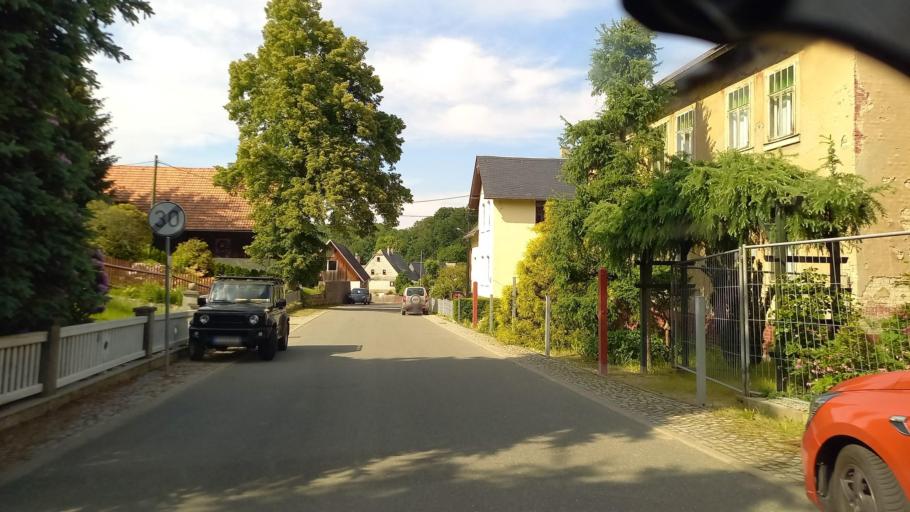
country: DE
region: Saxony
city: Wildenfels
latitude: 50.6326
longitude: 12.5872
